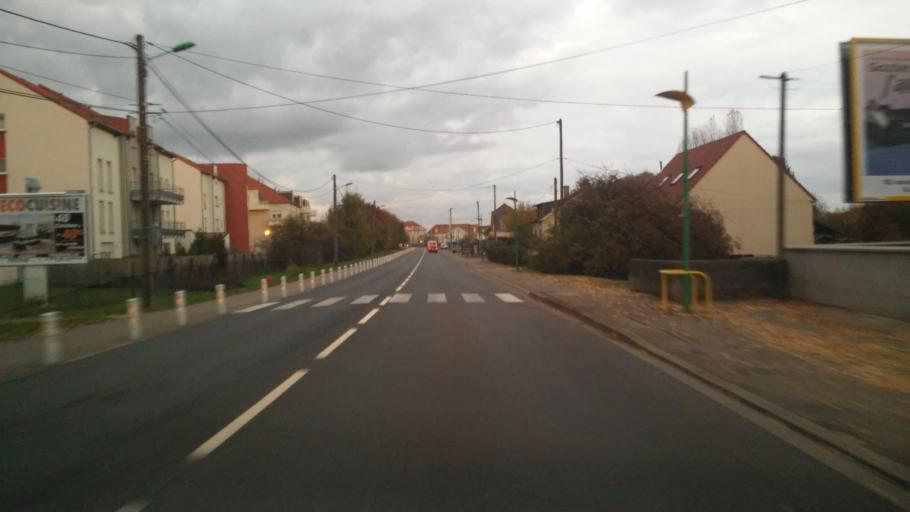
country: FR
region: Lorraine
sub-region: Departement de la Moselle
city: Talange
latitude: 49.2233
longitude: 6.1654
